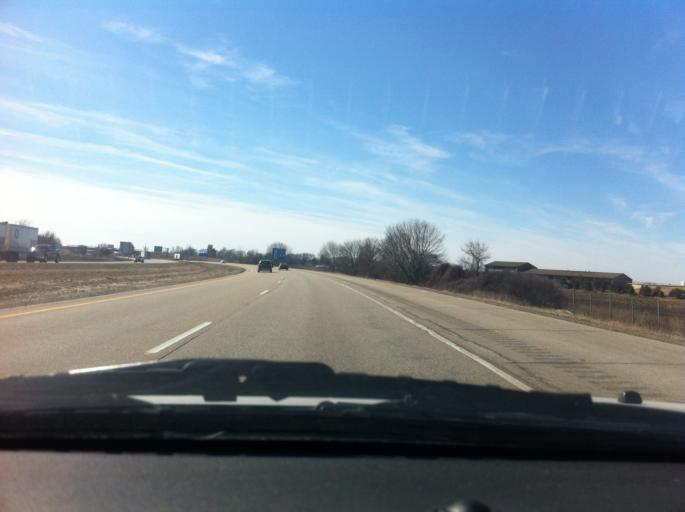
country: US
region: Wisconsin
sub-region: Rock County
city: Beloit
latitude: 42.5641
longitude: -88.9791
